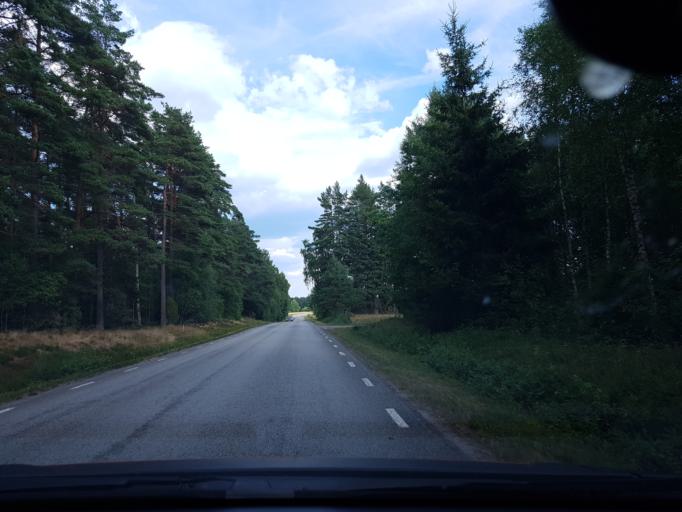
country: SE
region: Joenkoeping
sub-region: Gislaveds Kommun
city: Reftele
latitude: 57.2335
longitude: 13.5588
